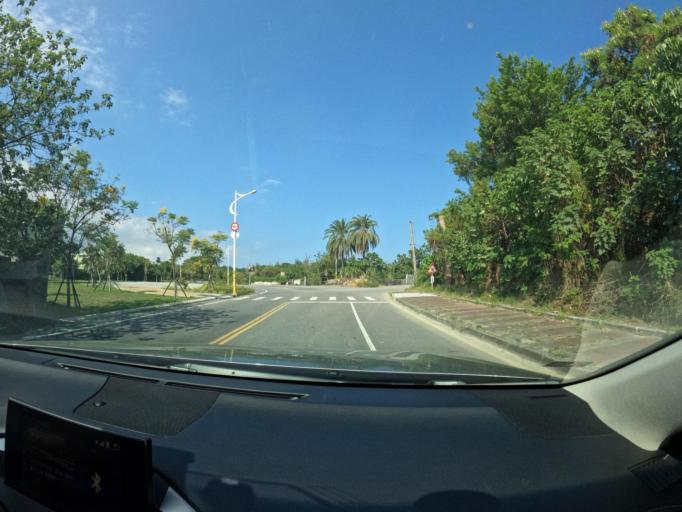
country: TW
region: Taiwan
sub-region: Hualien
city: Hualian
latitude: 24.0149
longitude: 121.6374
